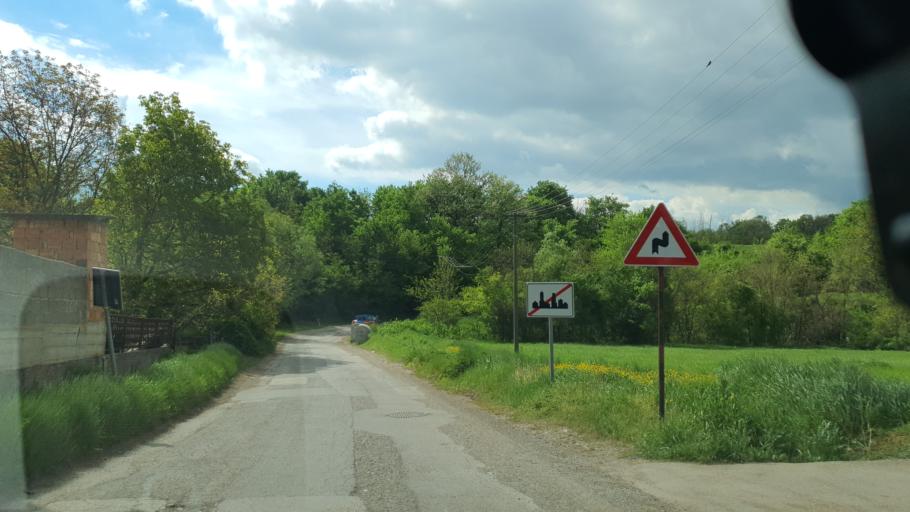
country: RS
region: Central Serbia
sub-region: Pomoravski Okrug
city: Paracin
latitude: 43.9368
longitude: 21.4930
